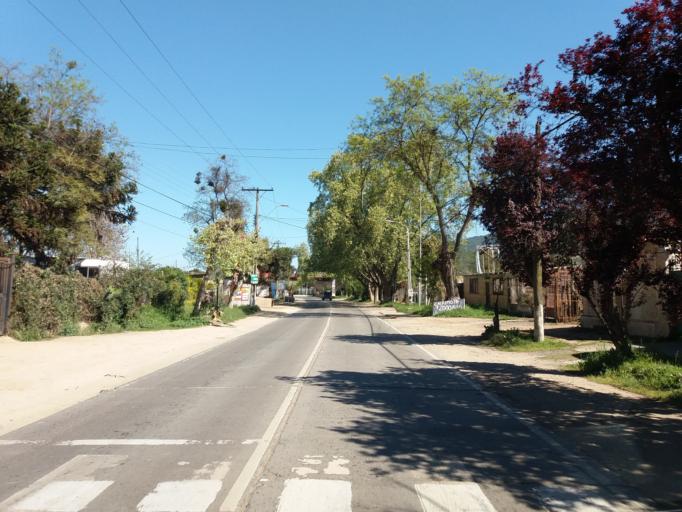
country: CL
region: Valparaiso
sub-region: Provincia de Marga Marga
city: Limache
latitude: -32.9979
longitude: -71.2184
